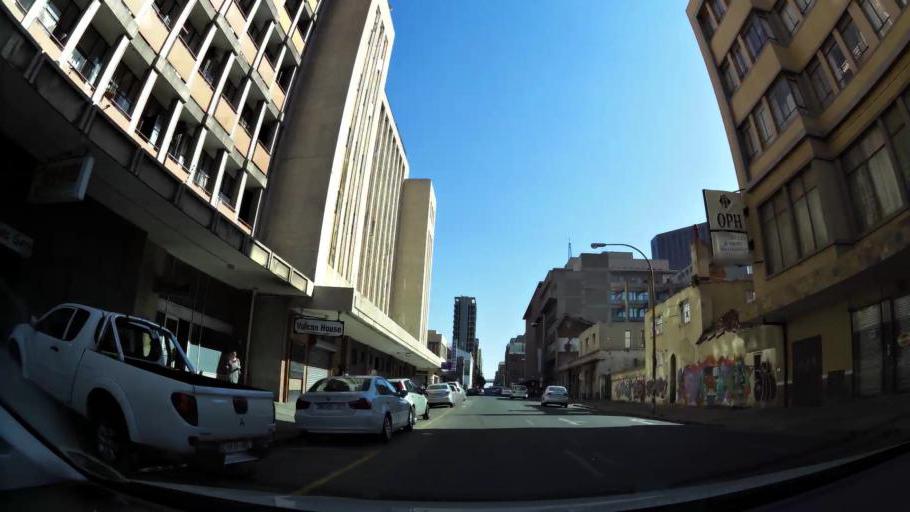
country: ZA
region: Gauteng
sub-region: City of Johannesburg Metropolitan Municipality
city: Johannesburg
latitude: -26.2079
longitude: 28.0440
